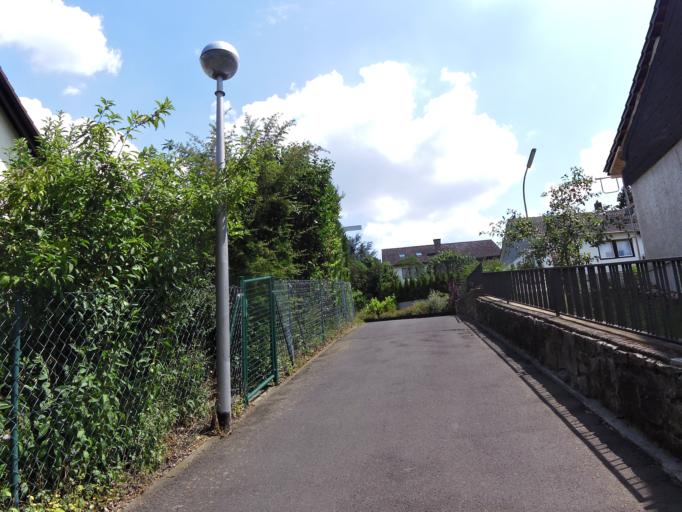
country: DE
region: Bavaria
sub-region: Regierungsbezirk Unterfranken
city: Randersacker
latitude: 49.7500
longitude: 9.9520
